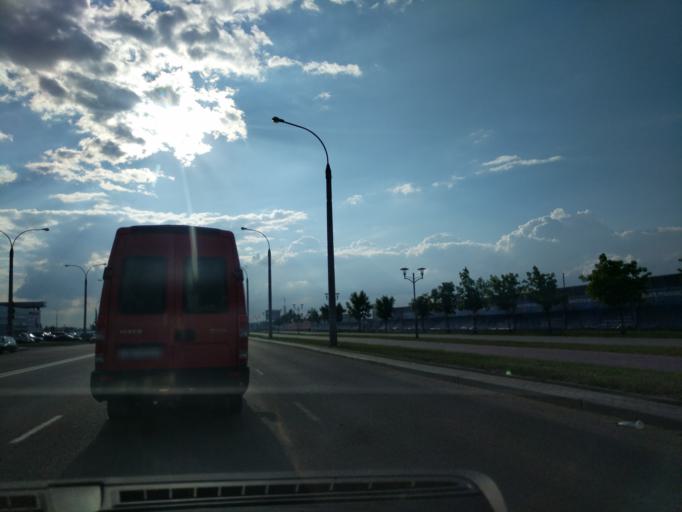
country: BY
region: Minsk
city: Zhdanovichy
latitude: 53.9172
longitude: 27.4214
